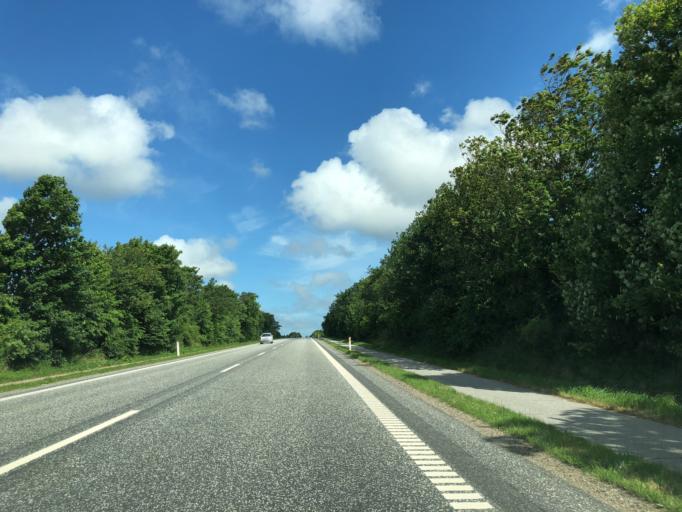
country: DK
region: Central Jutland
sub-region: Struer Kommune
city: Struer
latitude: 56.4594
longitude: 8.5904
